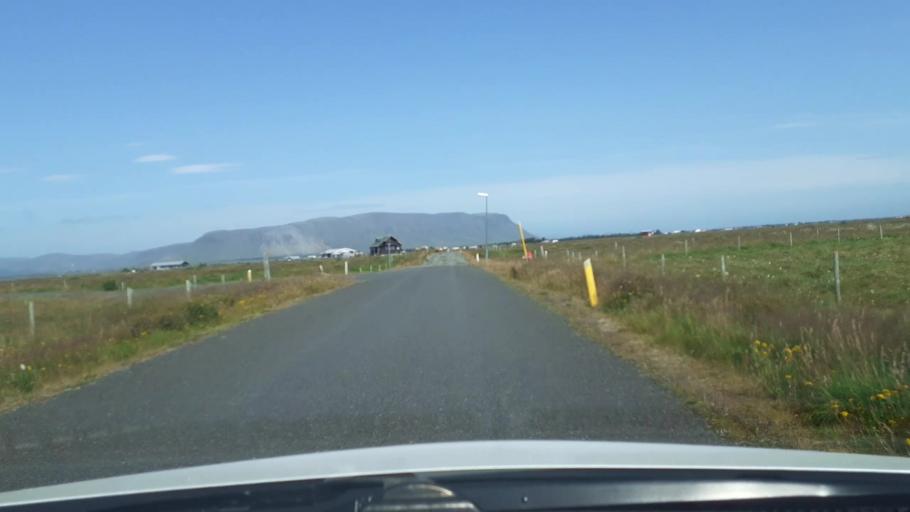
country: IS
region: South
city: Selfoss
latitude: 63.8957
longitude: -21.0810
